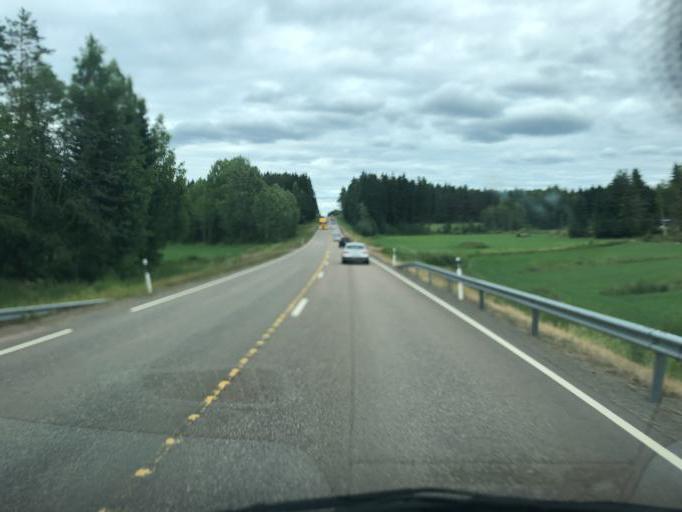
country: FI
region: Southern Savonia
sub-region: Mikkeli
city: Maentyharju
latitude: 61.0625
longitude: 27.0513
